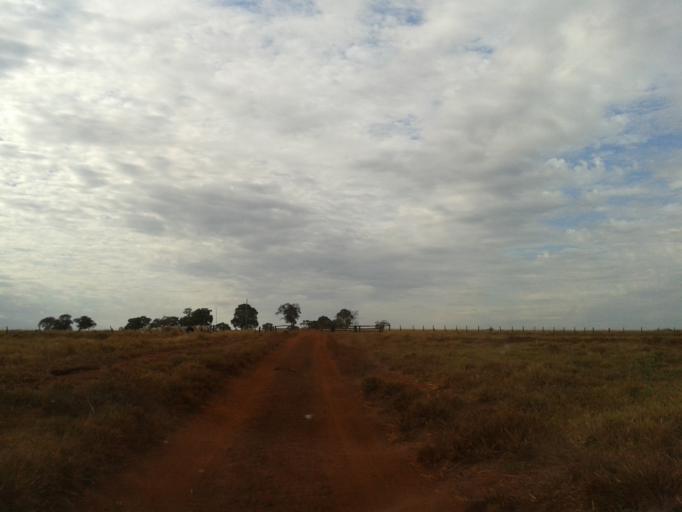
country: BR
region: Minas Gerais
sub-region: Santa Vitoria
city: Santa Vitoria
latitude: -18.7322
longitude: -50.2462
